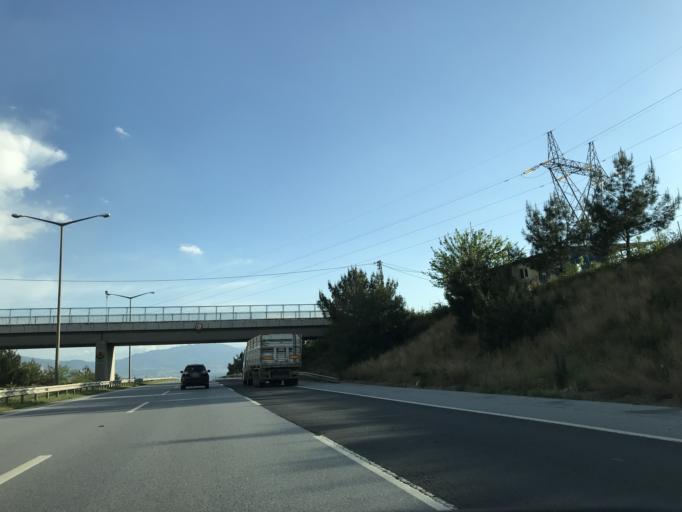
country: TR
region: Hatay
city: Yakacik
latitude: 36.7097
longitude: 36.2201
